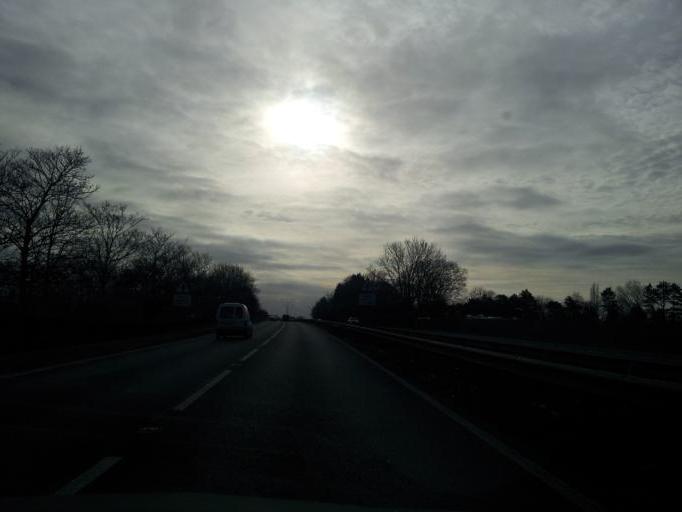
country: GB
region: England
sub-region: Peterborough
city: Wittering
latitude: 52.6155
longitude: -0.4458
